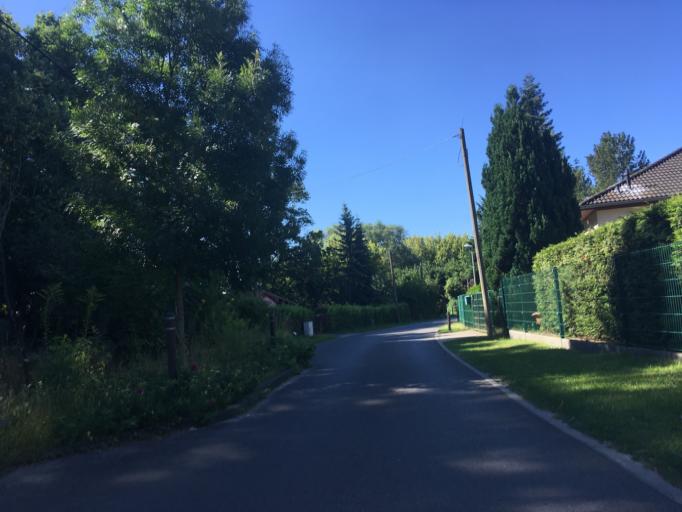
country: DE
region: Brandenburg
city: Altlandsberg
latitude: 52.5582
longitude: 13.7130
